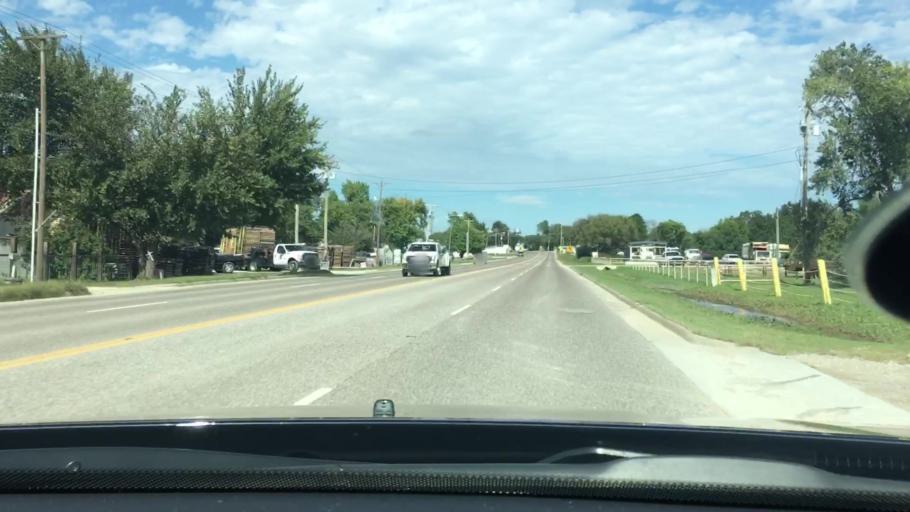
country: US
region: Oklahoma
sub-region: Murray County
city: Davis
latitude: 34.4951
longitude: -97.1269
